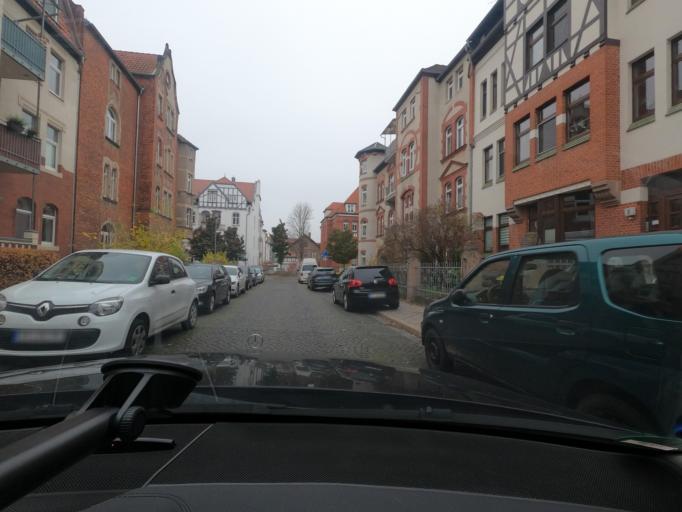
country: DE
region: Thuringia
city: Erfurt
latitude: 50.9657
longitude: 11.0378
